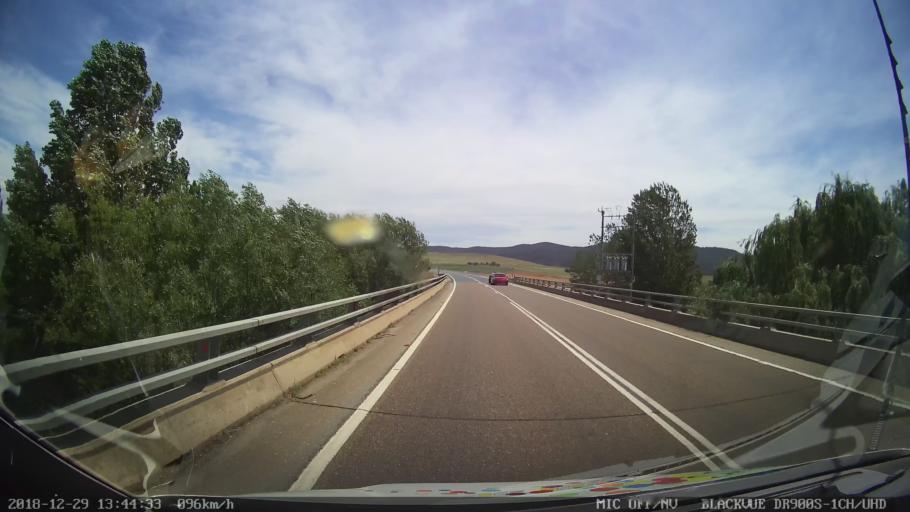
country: AU
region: New South Wales
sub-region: Cooma-Monaro
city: Cooma
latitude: -36.0845
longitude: 149.1505
